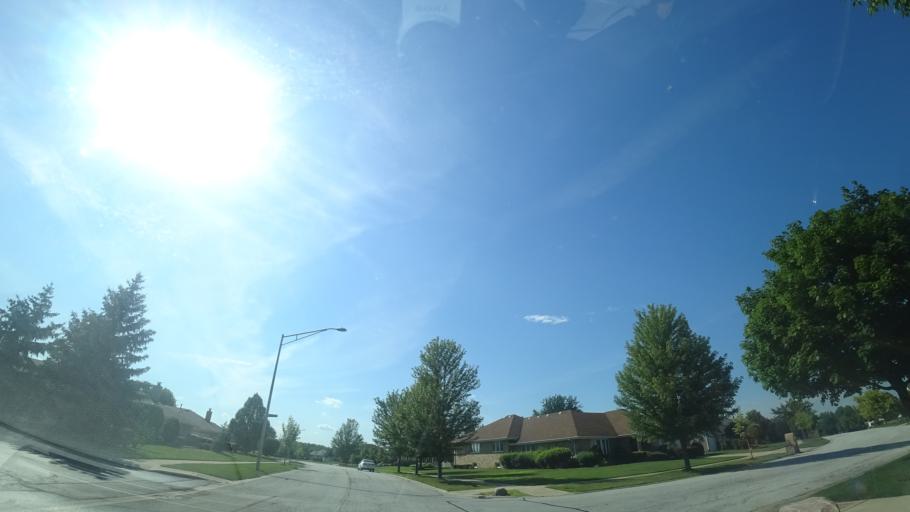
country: US
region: Illinois
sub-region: Will County
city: Mokena
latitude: 41.5682
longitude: -87.8840
